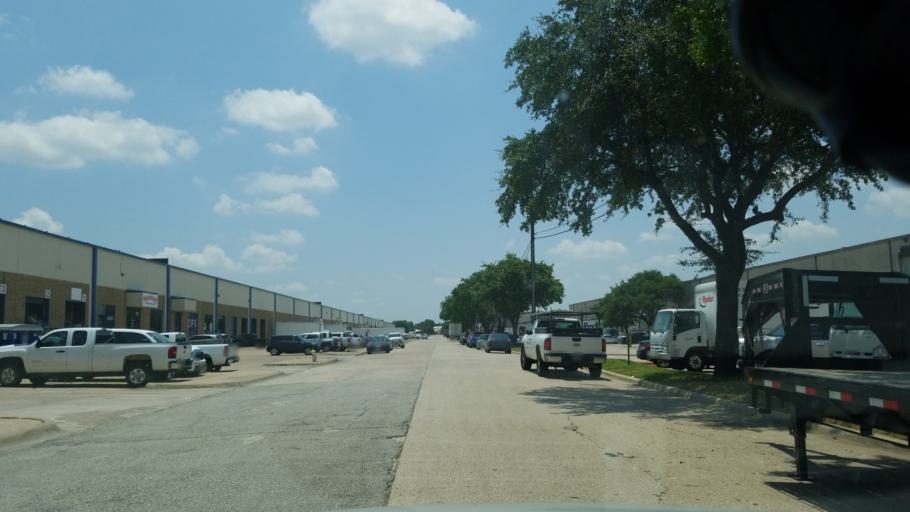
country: US
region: Texas
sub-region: Dallas County
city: Carrollton
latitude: 32.9590
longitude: -96.8795
